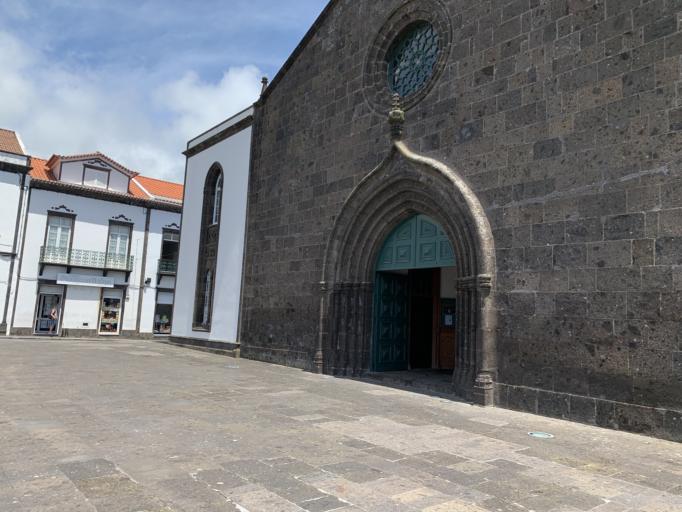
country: PT
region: Azores
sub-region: Vila Franca do Campo
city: Vila Franca do Campo
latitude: 37.7158
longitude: -25.4366
